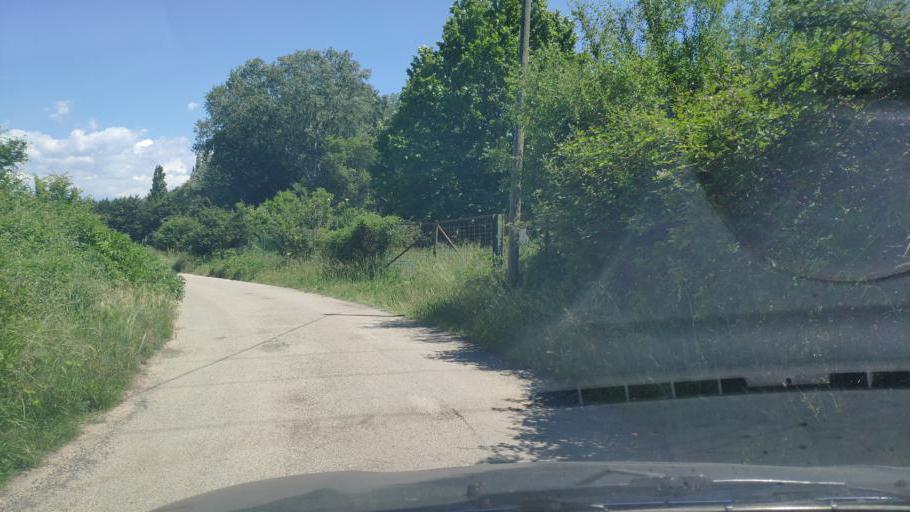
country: FR
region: Provence-Alpes-Cote d'Azur
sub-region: Departement du Vaucluse
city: Aubignan
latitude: 44.0867
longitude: 5.0565
